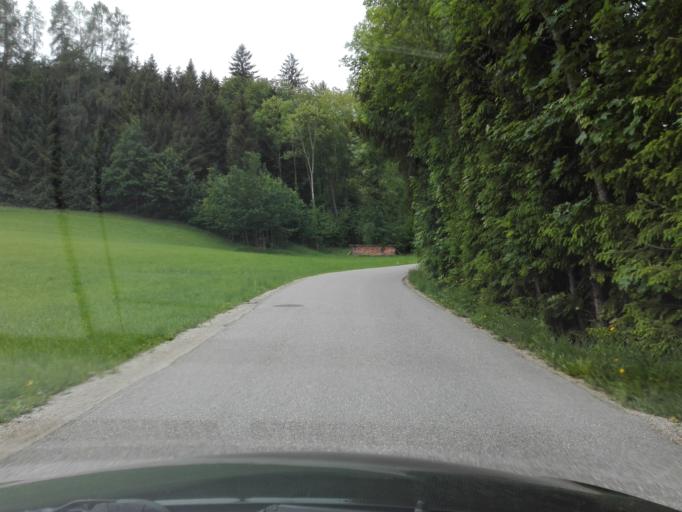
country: AT
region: Upper Austria
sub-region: Politischer Bezirk Gmunden
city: Scharnstein
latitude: 47.9230
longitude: 13.9696
